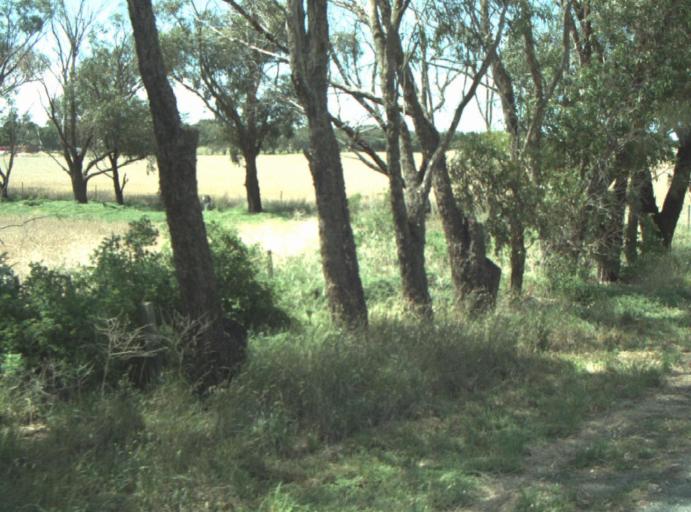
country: AU
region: Victoria
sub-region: Greater Geelong
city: Leopold
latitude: -38.1673
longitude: 144.4725
